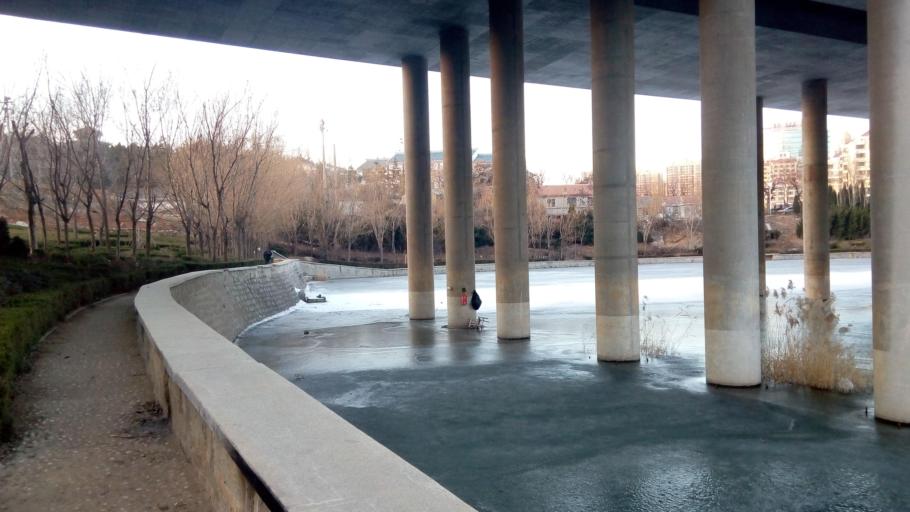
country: CN
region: Shandong Sheng
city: Xiangyang
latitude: 37.5222
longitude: 121.3886
